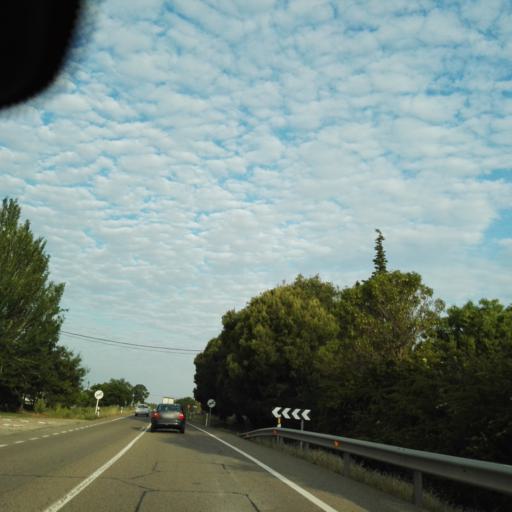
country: ES
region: Aragon
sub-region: Provincia de Zaragoza
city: Oliver-Valdefierro, Oliver, Valdefierro
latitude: 41.6638
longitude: -0.9676
